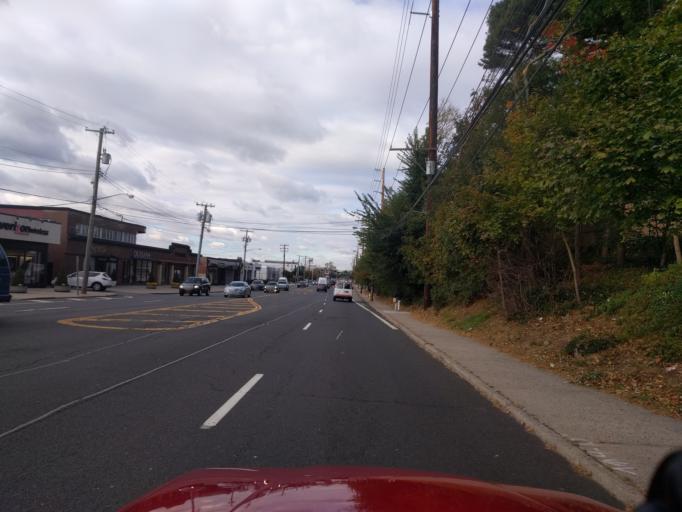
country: US
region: New York
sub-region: Nassau County
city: Manhasset
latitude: 40.7940
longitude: -73.6897
